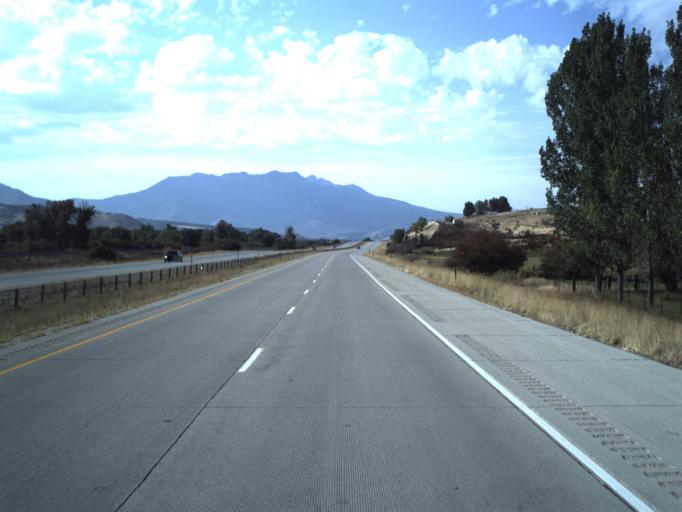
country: US
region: Utah
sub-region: Morgan County
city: Morgan
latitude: 41.0796
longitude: -111.7254
